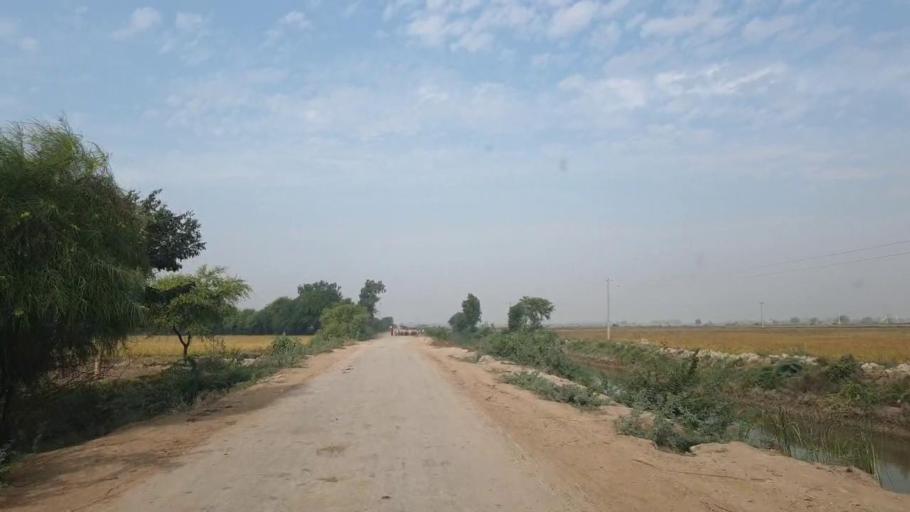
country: PK
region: Sindh
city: Tando Bago
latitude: 24.8631
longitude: 68.9961
